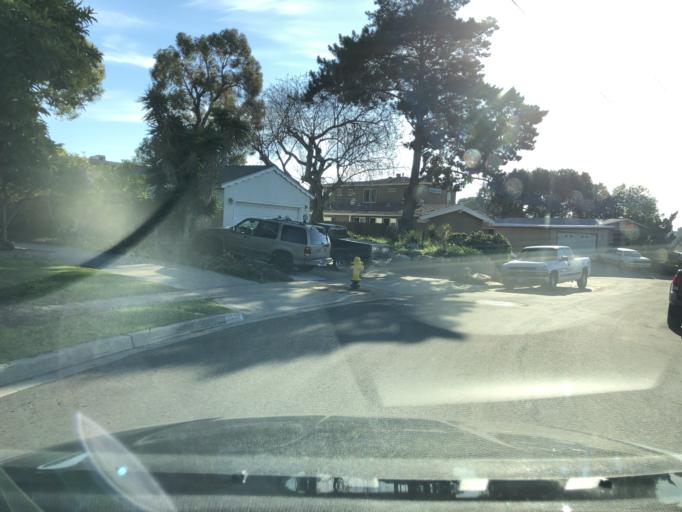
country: US
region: California
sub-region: San Diego County
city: La Jolla
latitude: 32.8212
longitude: -117.1973
